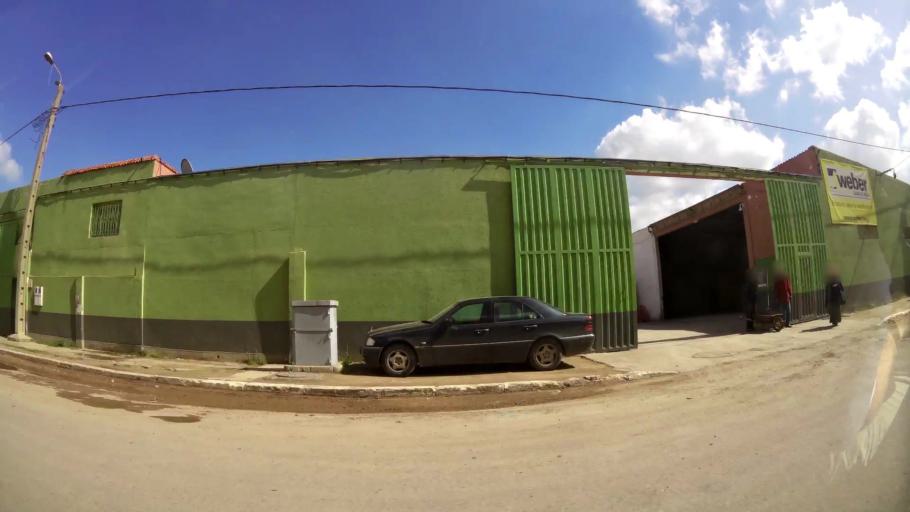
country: MA
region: Grand Casablanca
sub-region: Mediouna
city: Mediouna
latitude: 33.4557
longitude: -7.5135
